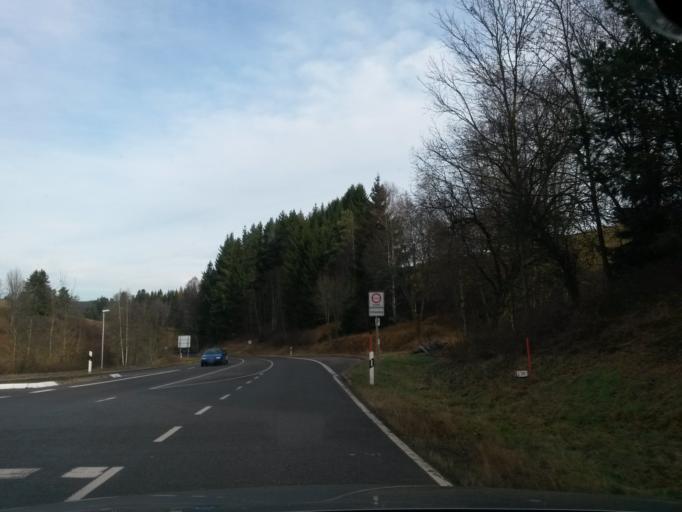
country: DE
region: Baden-Wuerttemberg
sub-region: Freiburg Region
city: Sankt Georgen im Schwarzwald
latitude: 48.1562
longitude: 8.3272
